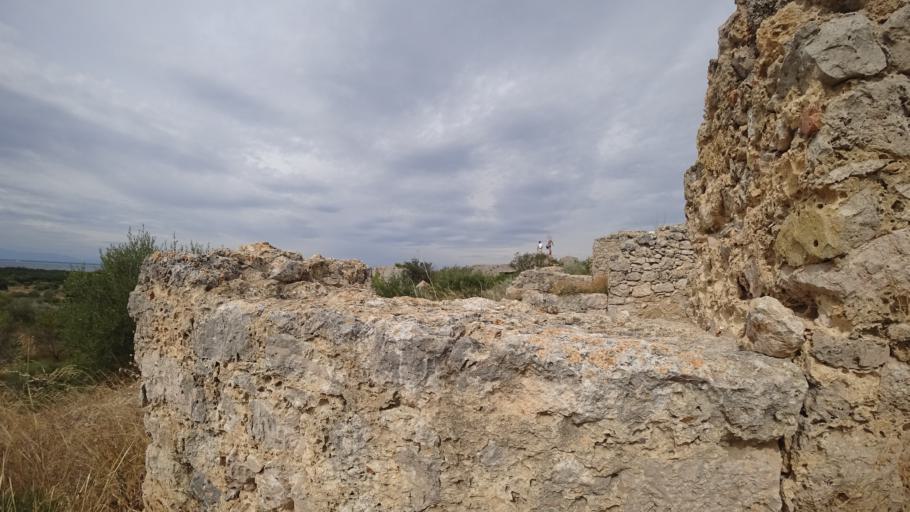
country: FR
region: Languedoc-Roussillon
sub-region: Departement de l'Aude
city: Leucate
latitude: 42.9076
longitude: 3.0251
